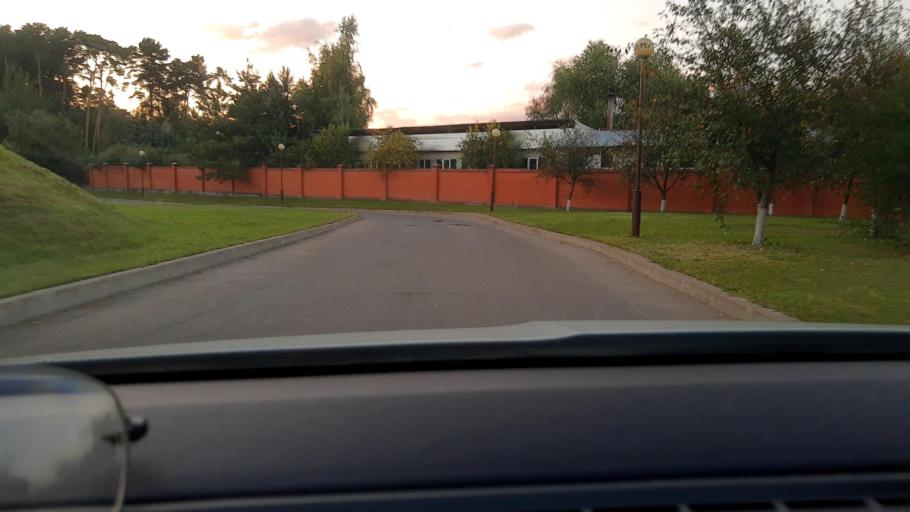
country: RU
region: Moskovskaya
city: Zarech'ye
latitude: 55.6805
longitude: 37.3903
